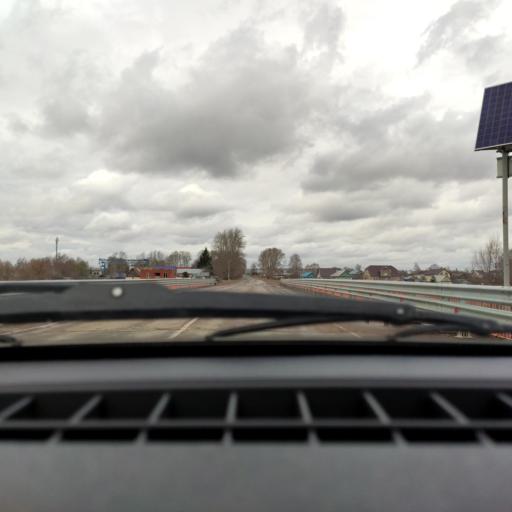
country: RU
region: Bashkortostan
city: Asanovo
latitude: 54.9558
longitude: 55.5544
